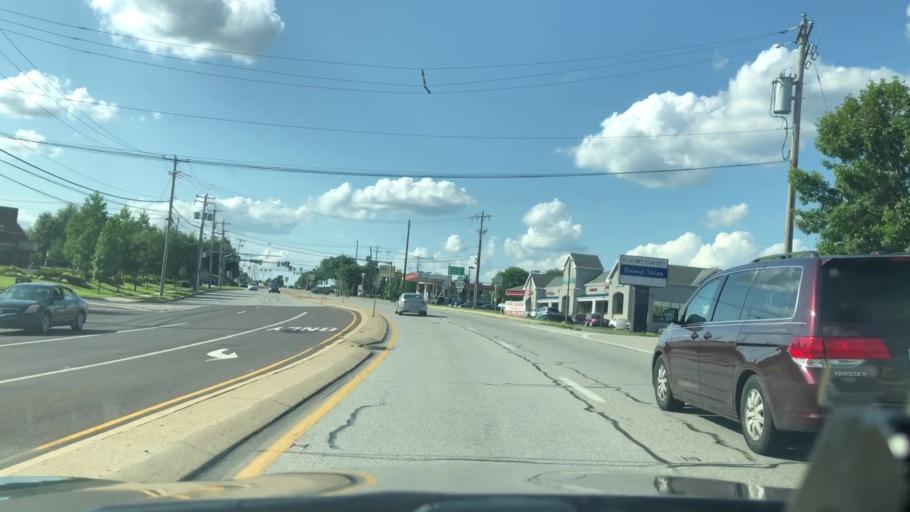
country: US
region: Pennsylvania
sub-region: Montgomery County
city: Montgomeryville
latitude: 40.2336
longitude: -75.2388
